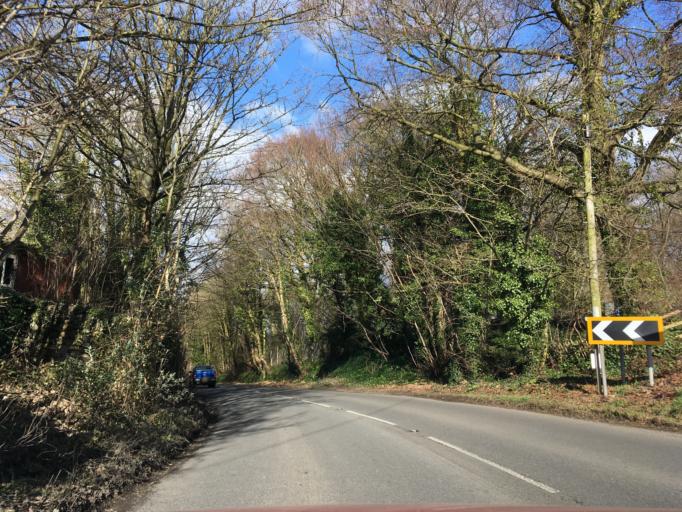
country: GB
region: England
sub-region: South Gloucestershire
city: Almondsbury
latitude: 51.5314
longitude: -2.6086
